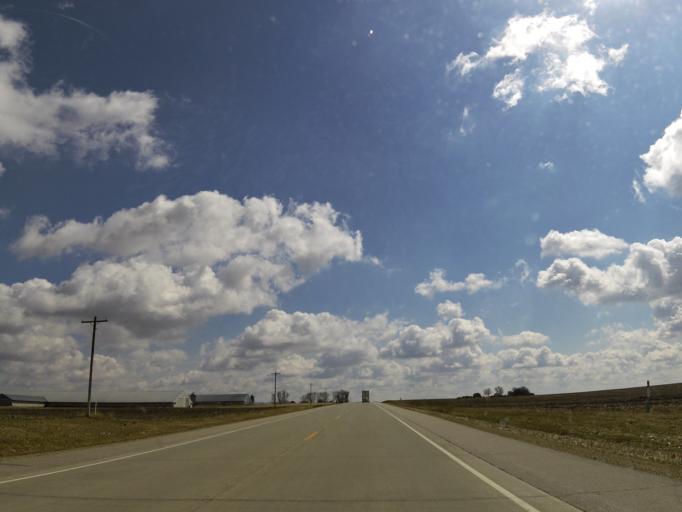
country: US
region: Minnesota
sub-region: Dodge County
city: Dodge Center
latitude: 44.1113
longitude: -92.8996
